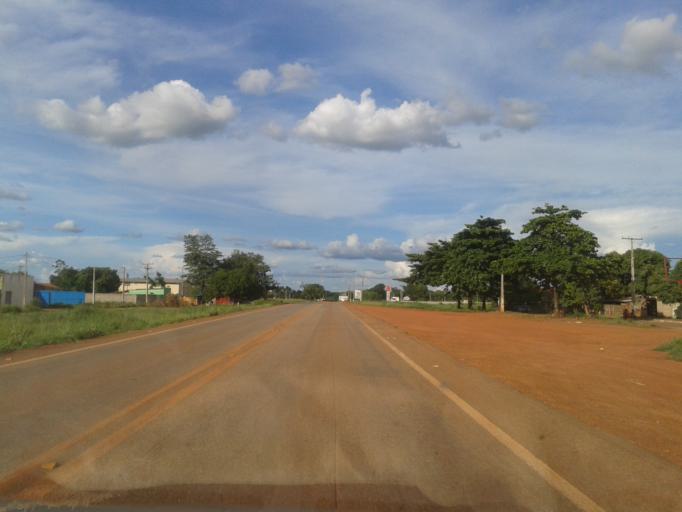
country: BR
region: Goias
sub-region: Crixas
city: Crixas
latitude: -14.1128
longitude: -50.3432
